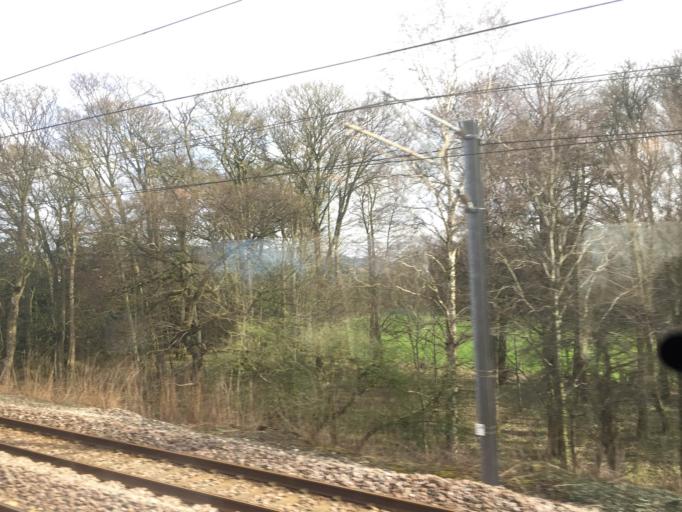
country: GB
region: England
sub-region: Cumbria
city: Penrith
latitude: 54.6506
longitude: -2.7670
